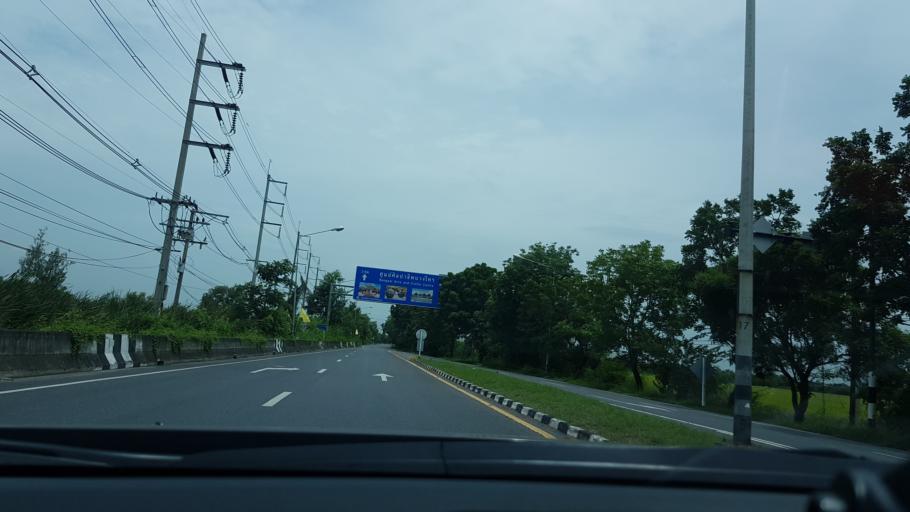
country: TH
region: Pathum Thani
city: Sam Khok
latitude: 14.1299
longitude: 100.5376
